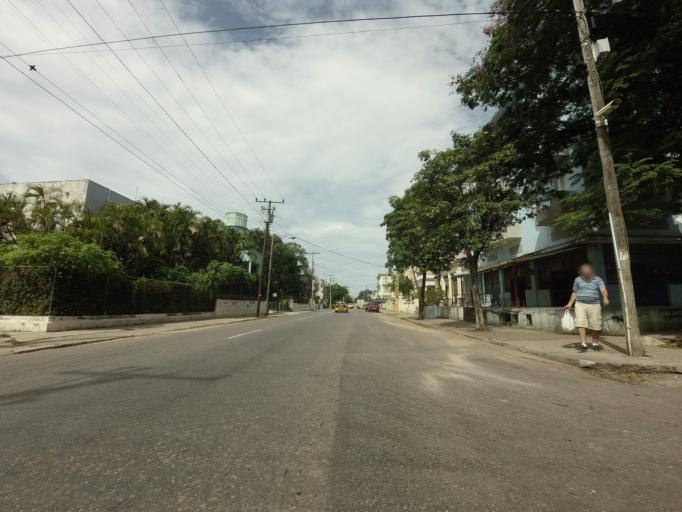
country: CU
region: La Habana
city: Havana
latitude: 23.1293
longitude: -82.4027
